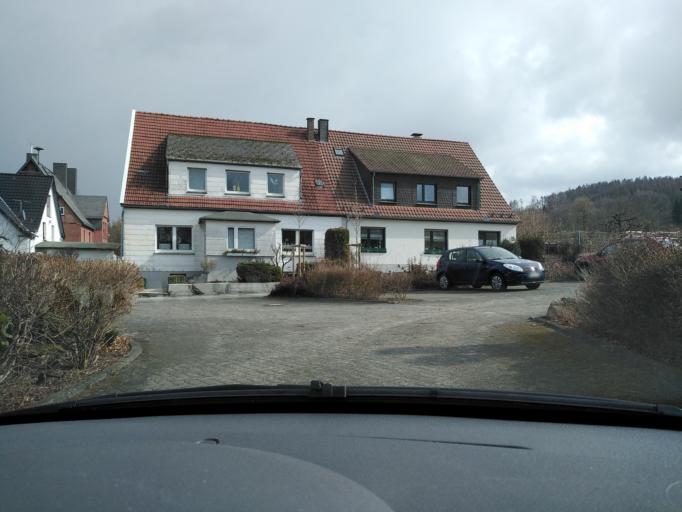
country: DE
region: North Rhine-Westphalia
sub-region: Regierungsbezirk Arnsberg
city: Brilon
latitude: 51.3758
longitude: 8.6390
